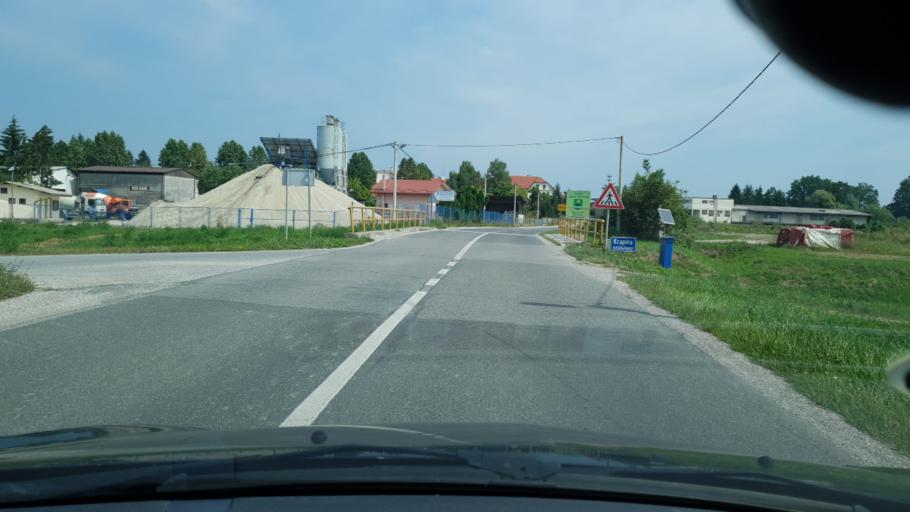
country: HR
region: Krapinsko-Zagorska
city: Marija Bistrica
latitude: 46.0421
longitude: 16.0825
